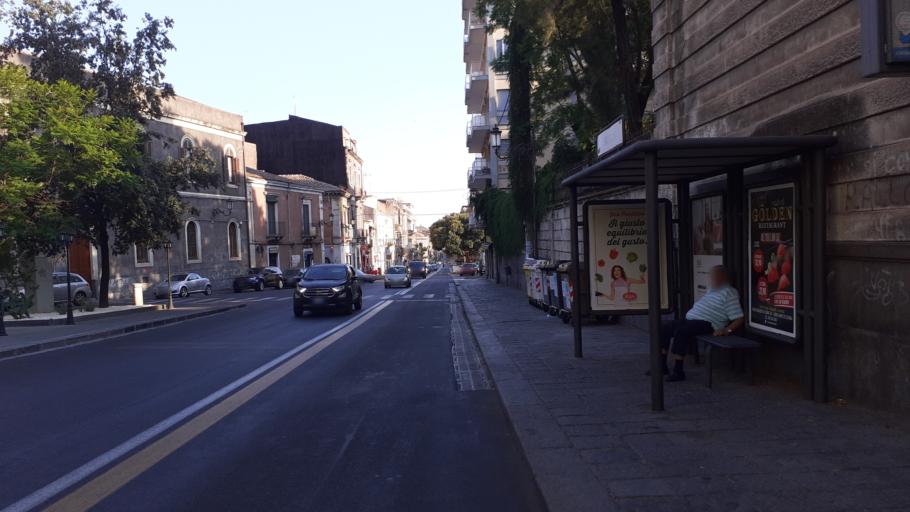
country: IT
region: Sicily
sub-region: Catania
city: Canalicchio
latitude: 37.5205
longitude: 15.0830
